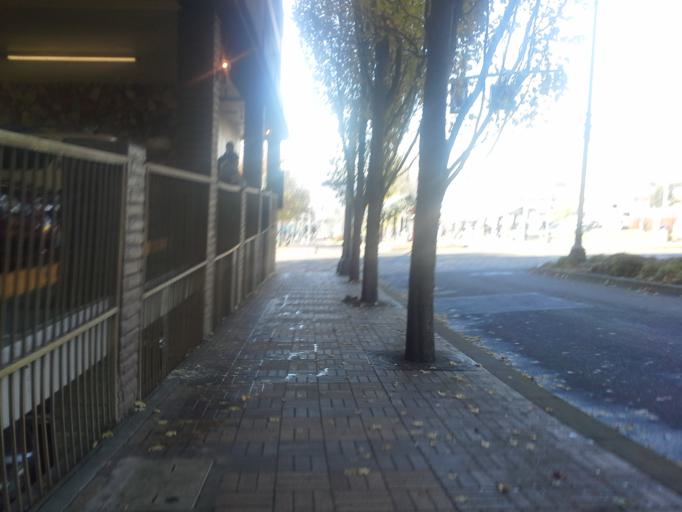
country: US
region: Oregon
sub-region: Multnomah County
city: Portland
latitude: 45.5300
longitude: -122.6611
